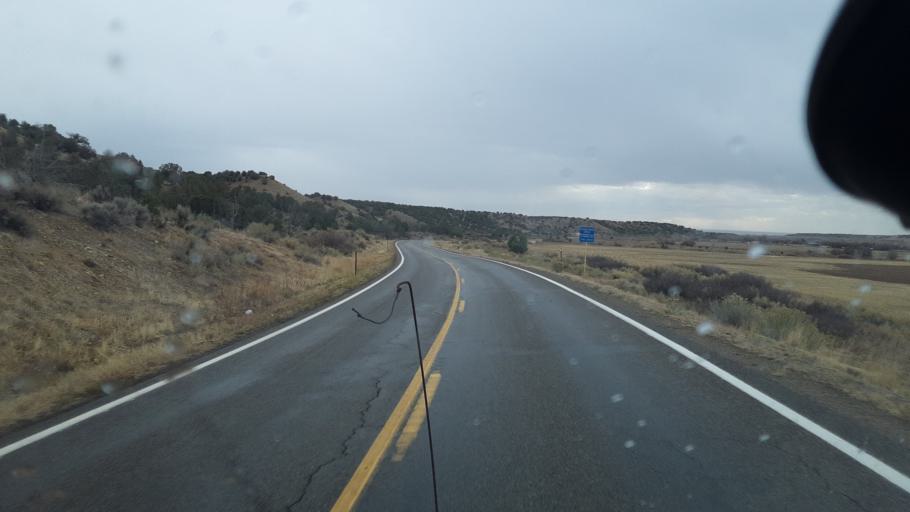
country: US
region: New Mexico
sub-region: San Juan County
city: Spencerville
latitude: 37.0181
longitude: -108.1835
